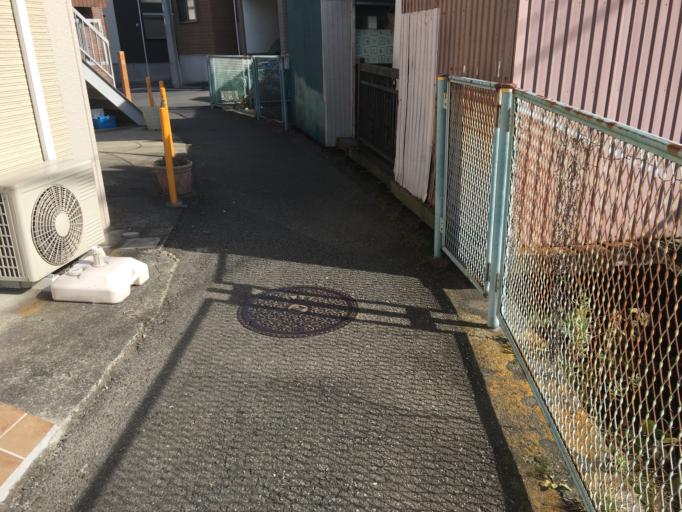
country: JP
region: Tokyo
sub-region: Machida-shi
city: Machida
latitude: 35.5138
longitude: 139.5423
